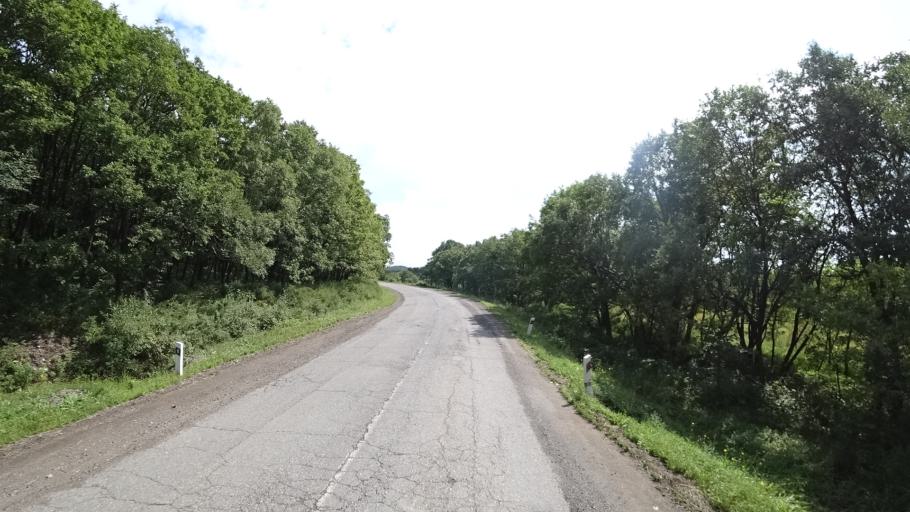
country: RU
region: Primorskiy
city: Lyalichi
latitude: 44.1500
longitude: 132.3932
